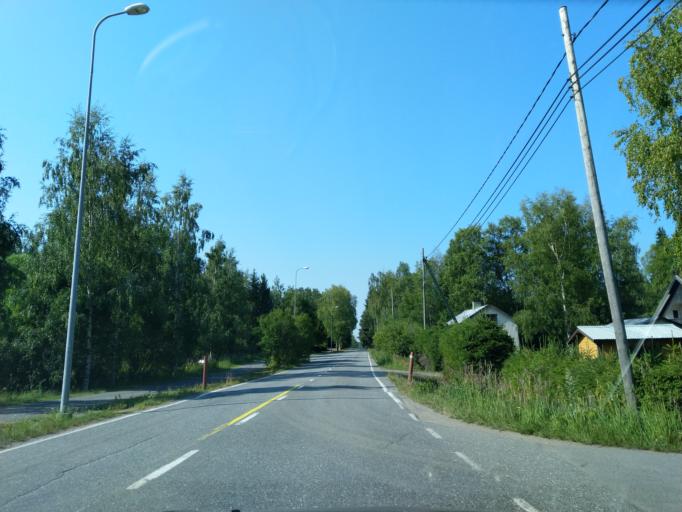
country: FI
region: Satakunta
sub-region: Pori
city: Pomarkku
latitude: 61.7049
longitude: 22.0255
